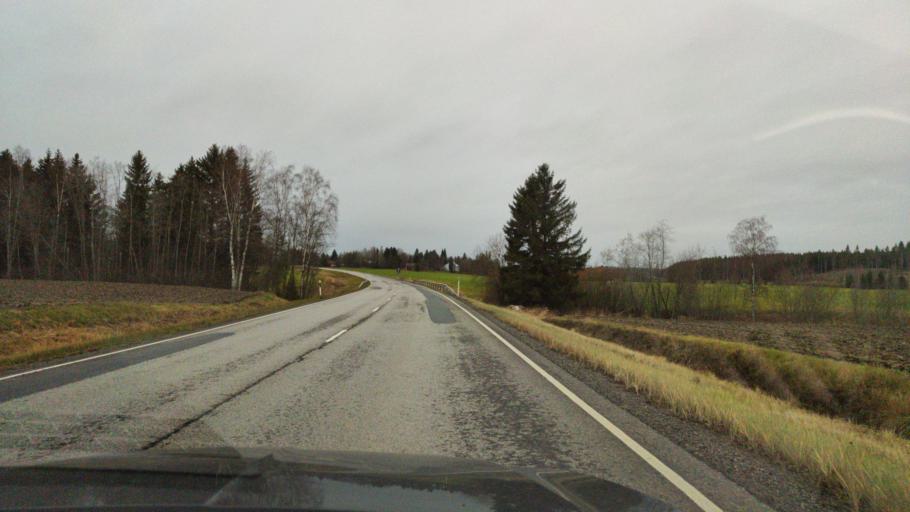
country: FI
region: Varsinais-Suomi
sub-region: Loimaa
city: Ylaene
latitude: 60.8508
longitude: 22.4353
